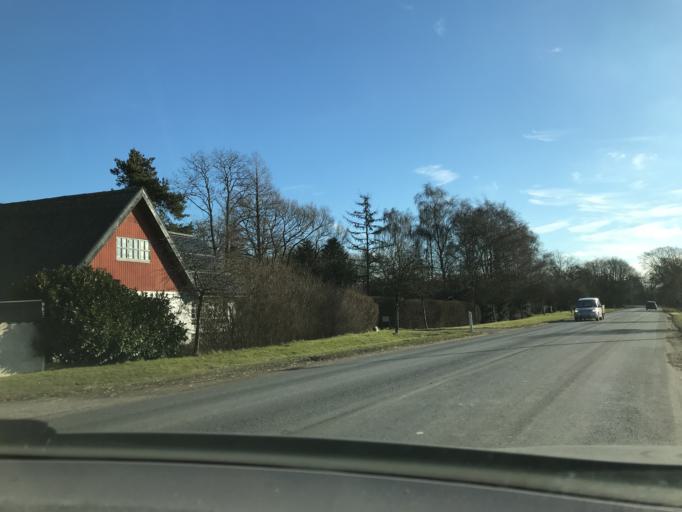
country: DK
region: South Denmark
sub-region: Middelfart Kommune
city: Strib
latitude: 55.5031
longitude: 9.7924
